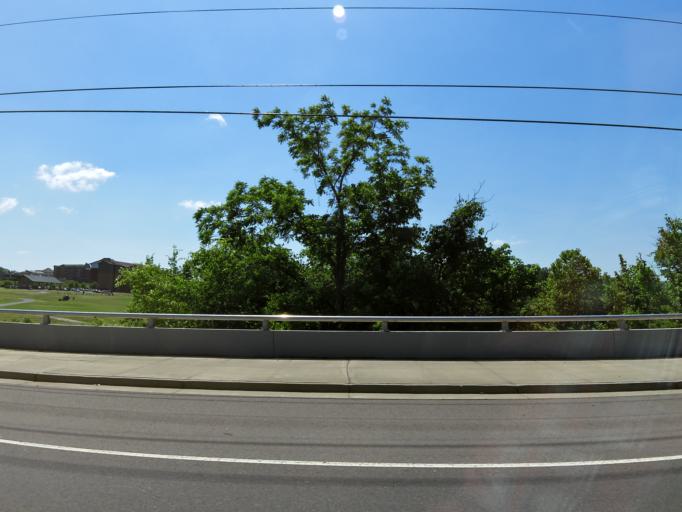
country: US
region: Tennessee
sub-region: Sevier County
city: Sevierville
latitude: 35.8980
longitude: -83.5812
